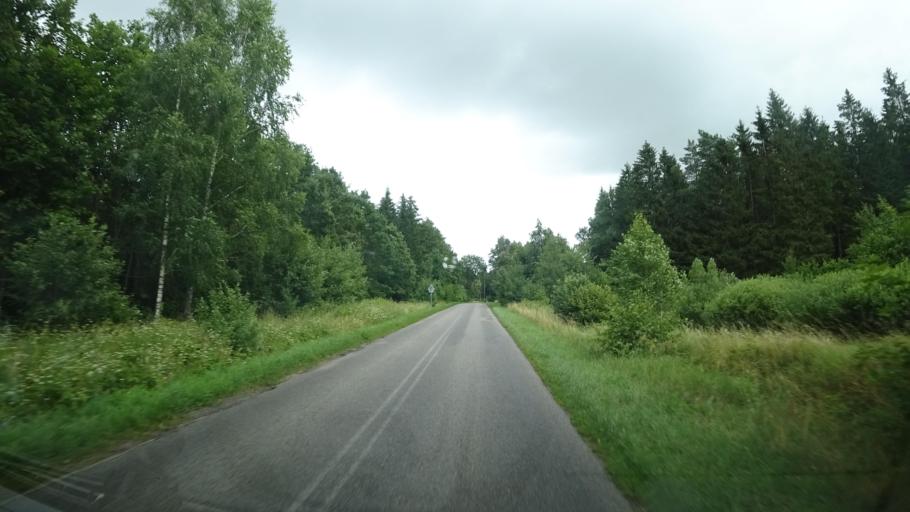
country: PL
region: Warmian-Masurian Voivodeship
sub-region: Powiat goldapski
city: Goldap
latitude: 54.3091
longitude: 22.3921
